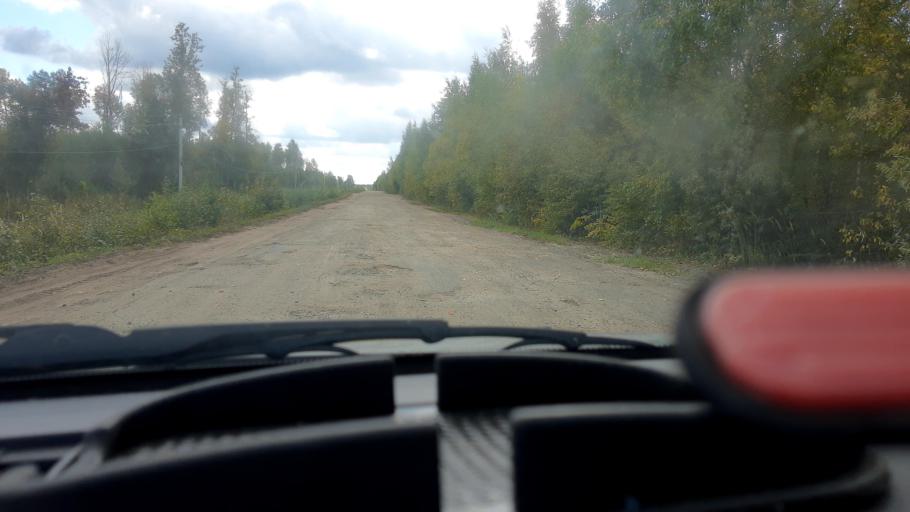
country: RU
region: Mariy-El
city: Kilemary
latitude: 56.8958
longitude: 46.7494
